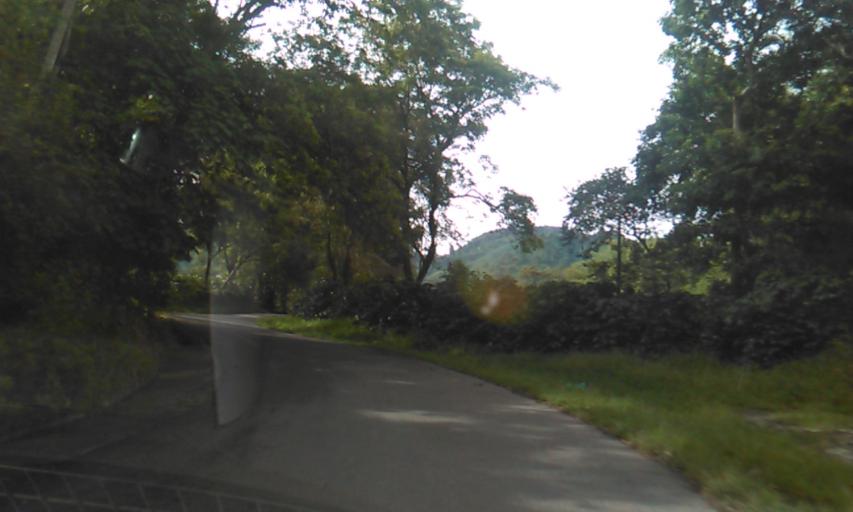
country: CO
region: Quindio
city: Cordoba
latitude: 4.4012
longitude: -75.6896
